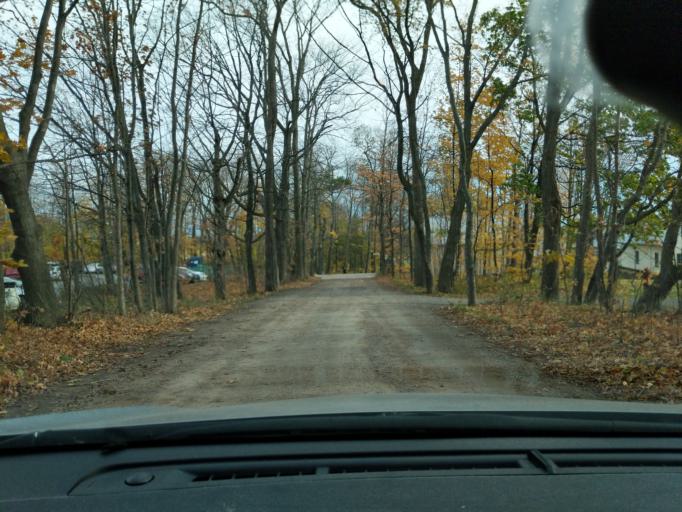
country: CA
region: Quebec
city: Quebec
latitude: 46.7744
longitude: -71.2536
